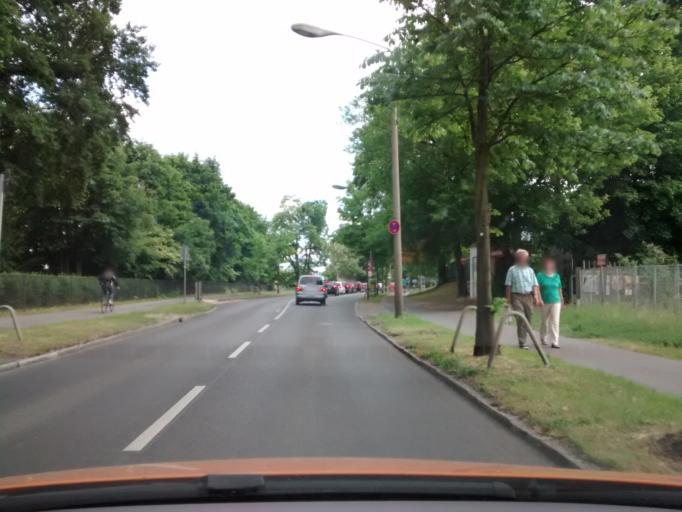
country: DE
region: Berlin
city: Grunau
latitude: 52.4071
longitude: 13.5736
